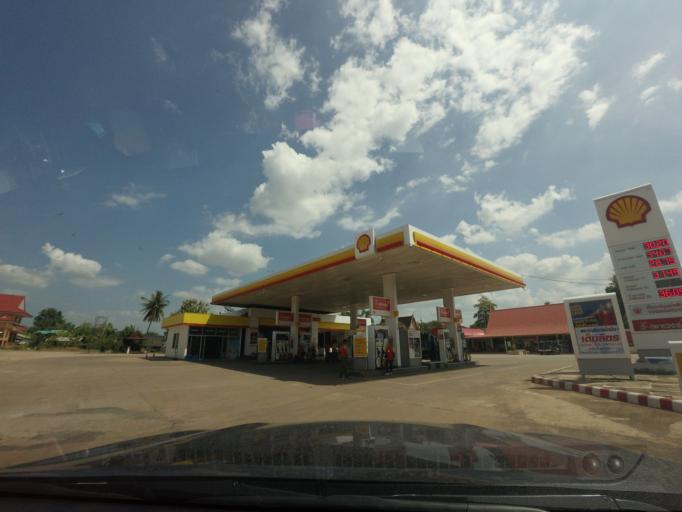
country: TH
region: Phetchabun
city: Nong Phai
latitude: 15.9113
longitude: 101.0271
